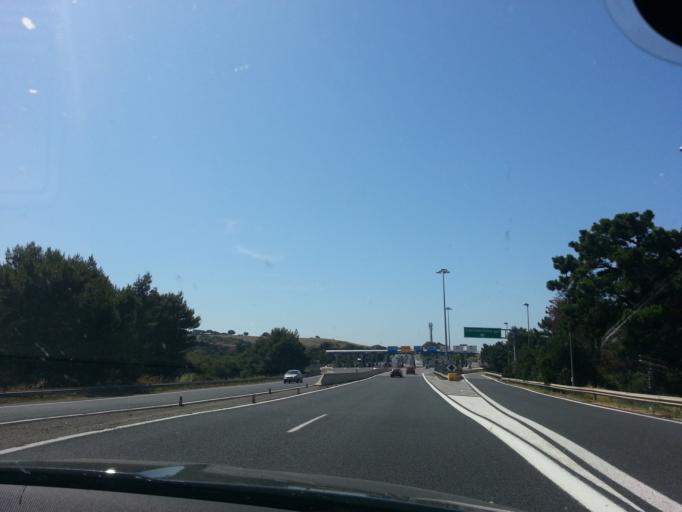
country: IT
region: Latium
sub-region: Citta metropolitana di Roma Capitale
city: Civitavecchia
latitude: 42.0613
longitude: 11.8235
